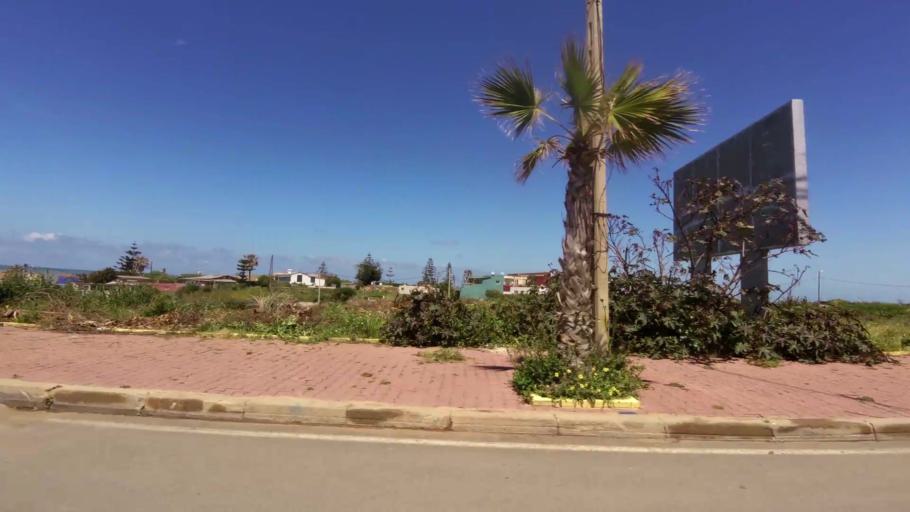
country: MA
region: Grand Casablanca
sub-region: Nouaceur
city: Dar Bouazza
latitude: 33.5331
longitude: -7.8256
